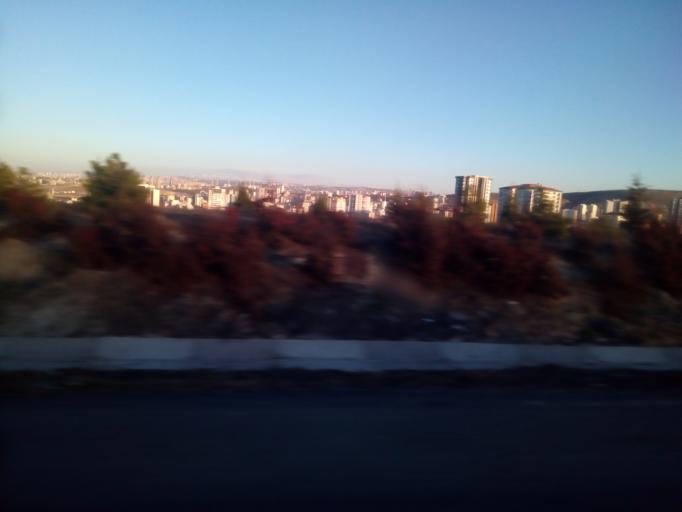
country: TR
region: Ankara
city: Etimesgut
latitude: 39.9054
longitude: 32.6263
